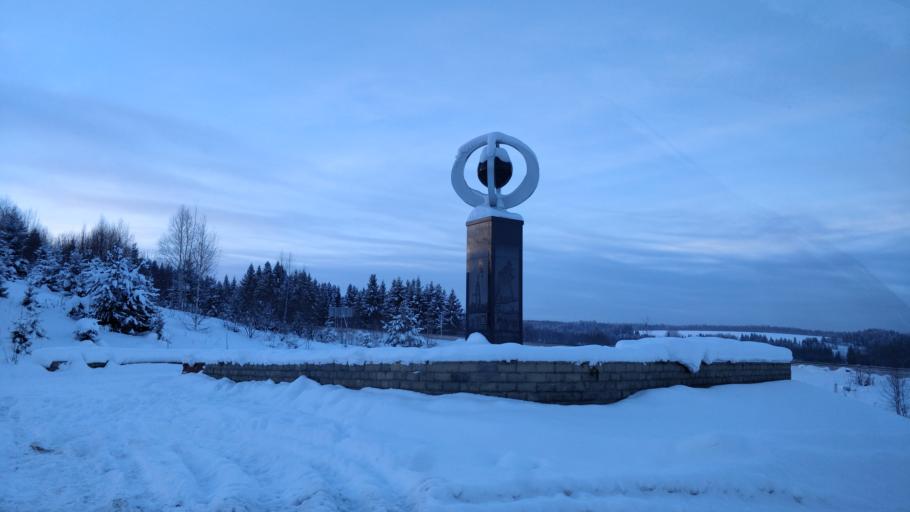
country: RU
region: Perm
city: Verkhnechusovskiye Gorodki
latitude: 58.2135
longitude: 57.1414
